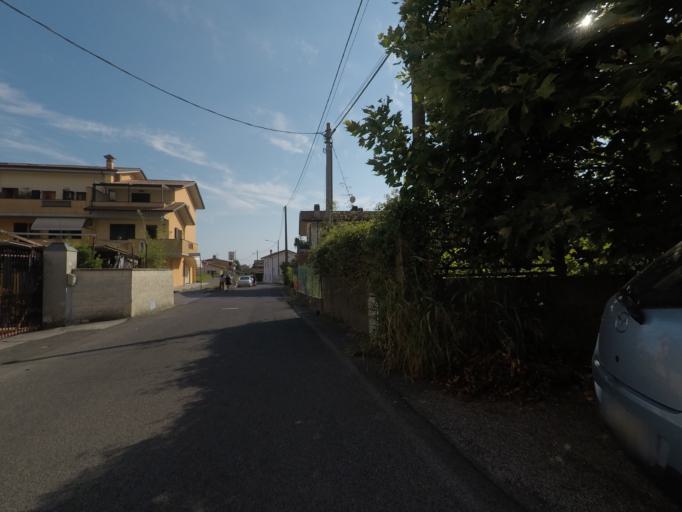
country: IT
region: Tuscany
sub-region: Provincia di Massa-Carrara
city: Capanne-Prato-Cinquale
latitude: 44.0049
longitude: 10.1565
